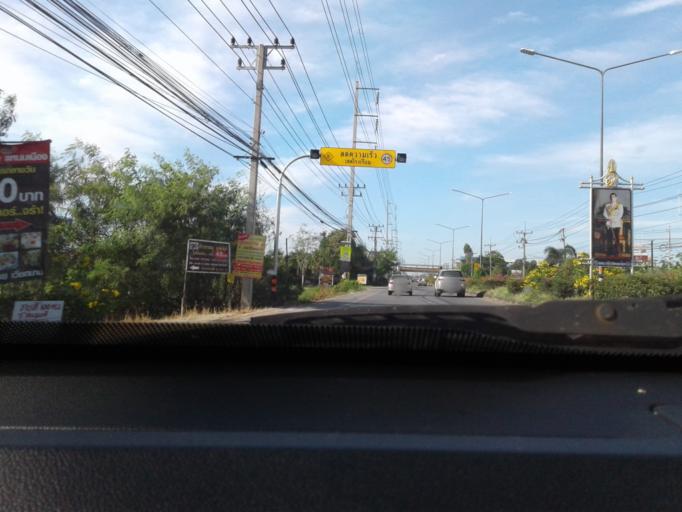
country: TH
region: Nakhon Pathom
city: Salaya
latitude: 13.8401
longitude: 100.3079
